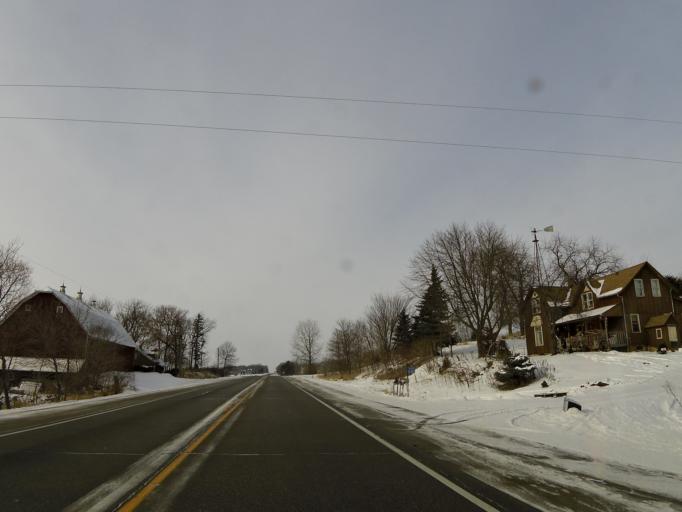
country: US
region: Minnesota
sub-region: Hennepin County
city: Saint Bonifacius
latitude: 44.9054
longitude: -93.7901
